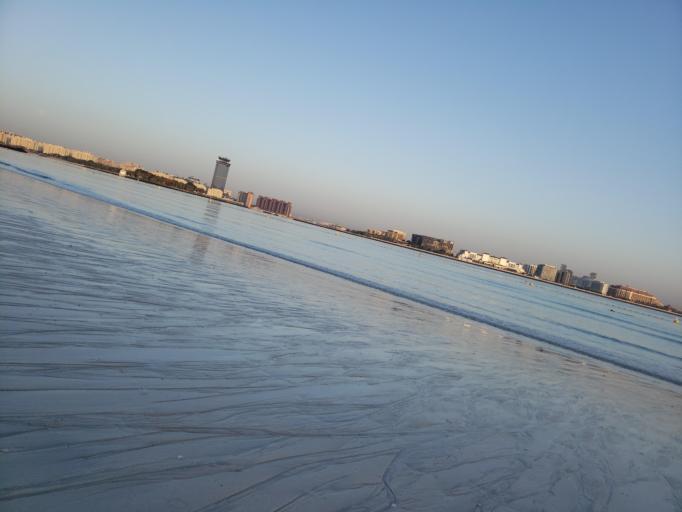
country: AE
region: Dubai
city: Dubai
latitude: 25.1191
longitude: 55.1691
